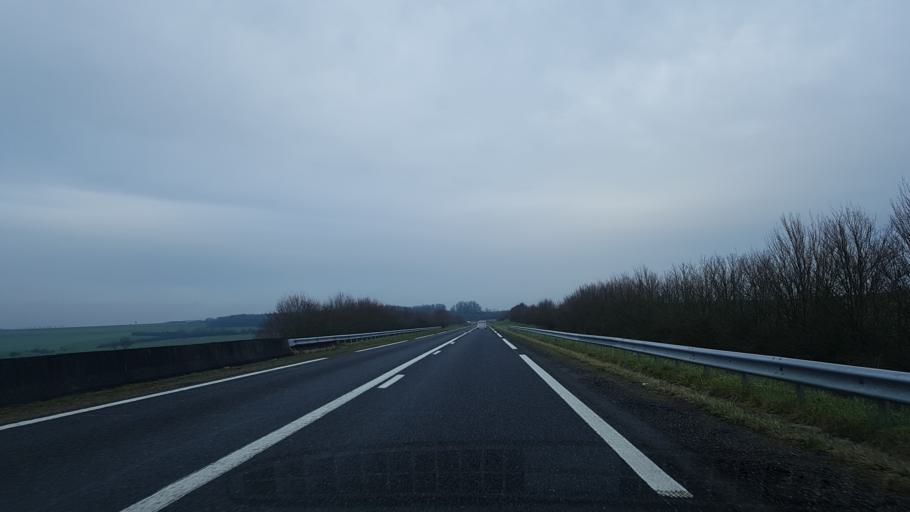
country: FR
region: Lorraine
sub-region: Departement de la Moselle
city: Gros-Rederching
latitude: 49.0944
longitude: 7.2477
